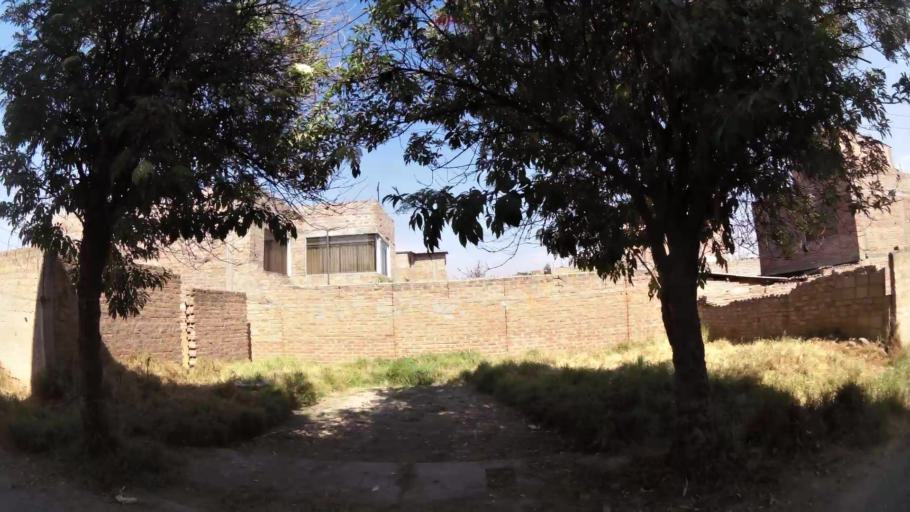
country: PE
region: Junin
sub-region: Provincia de Huancayo
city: El Tambo
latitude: -12.0737
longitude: -75.2286
